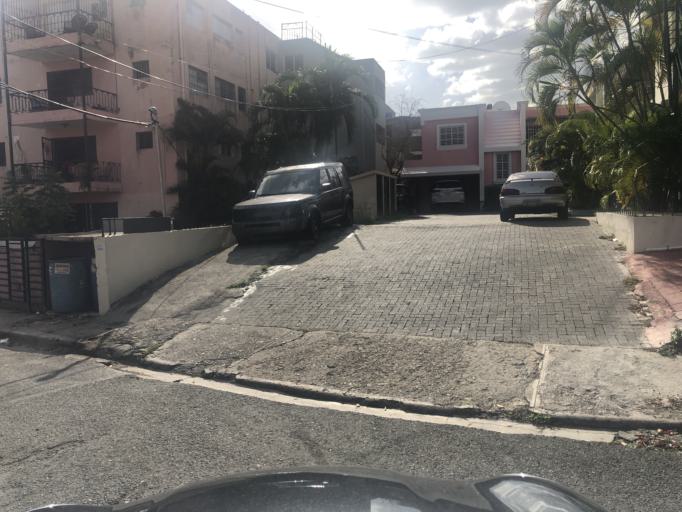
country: DO
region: Nacional
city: La Julia
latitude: 18.4556
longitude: -69.9280
